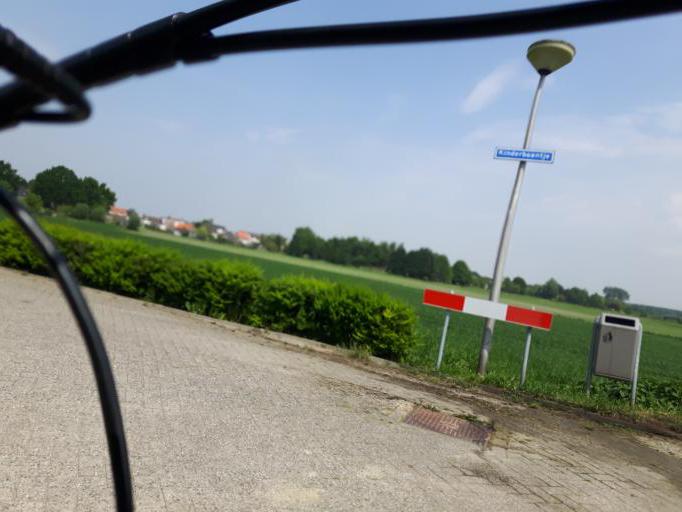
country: NL
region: North Brabant
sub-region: Gemeente Steenbergen
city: Welberg
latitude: 51.5758
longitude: 4.3348
